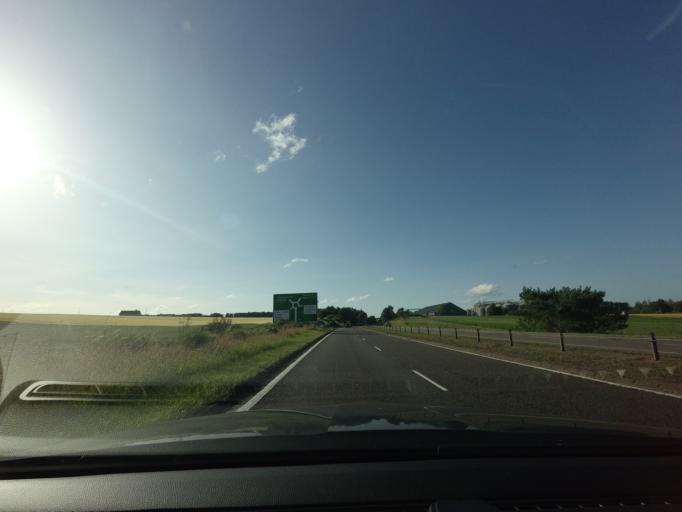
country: GB
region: Scotland
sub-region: Highland
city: Inverness
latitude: 57.5274
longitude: -4.3241
